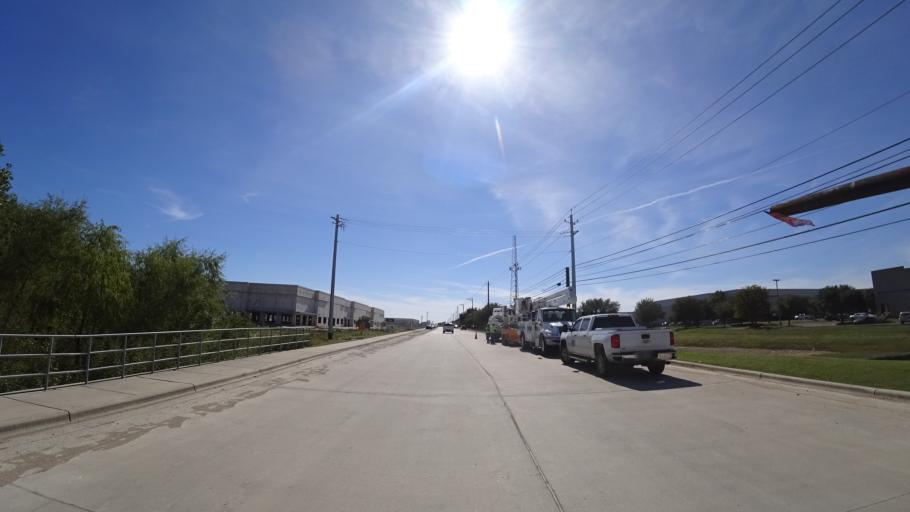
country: US
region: Texas
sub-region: Travis County
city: Austin
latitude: 30.2080
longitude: -97.7450
